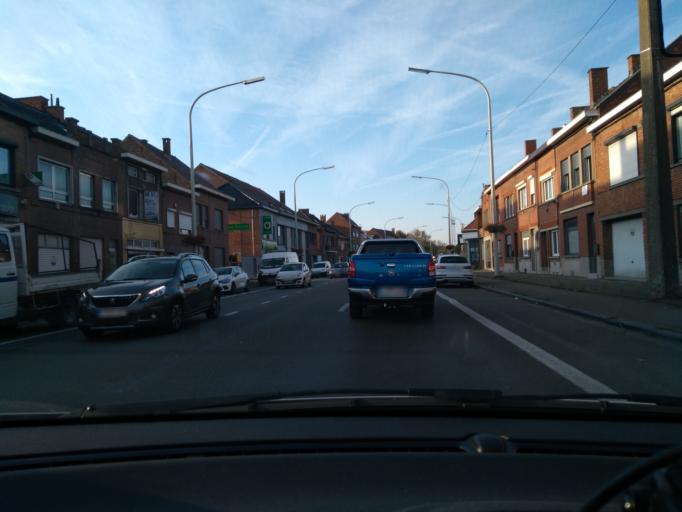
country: BE
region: Wallonia
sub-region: Province du Hainaut
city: Saint-Ghislain
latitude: 50.4388
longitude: 3.8257
